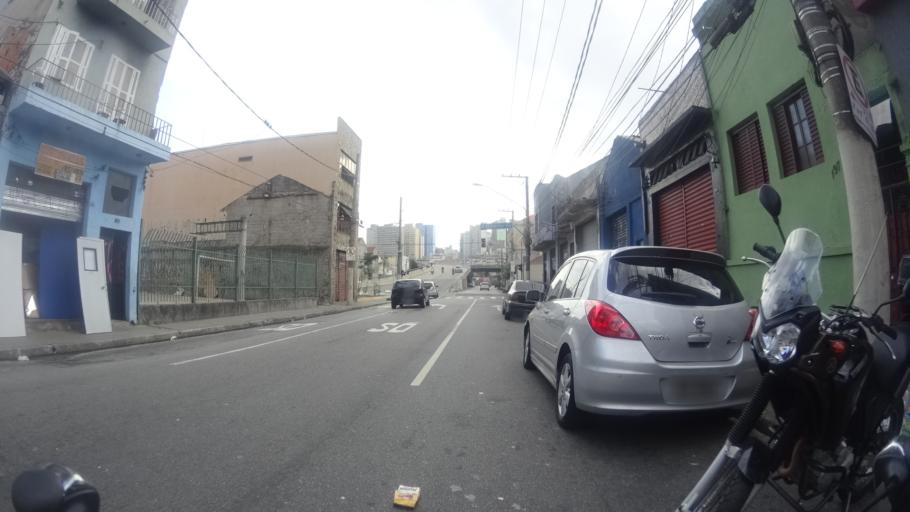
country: BR
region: Sao Paulo
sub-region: Sao Paulo
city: Sao Paulo
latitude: -23.5535
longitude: -46.6233
